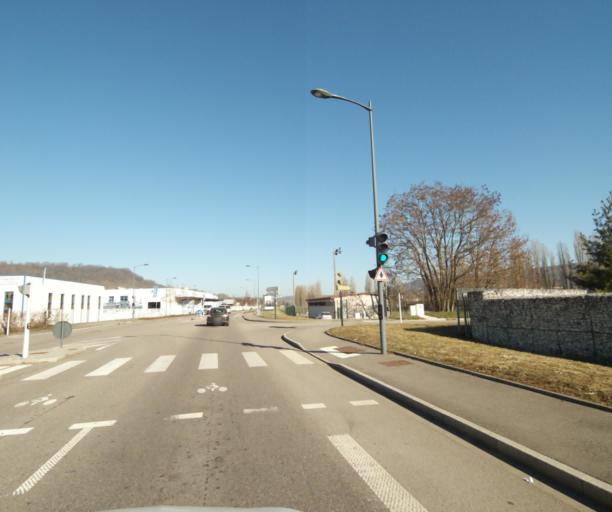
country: FR
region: Lorraine
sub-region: Departement de Meurthe-et-Moselle
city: Maxeville
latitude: 48.7130
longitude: 6.1723
